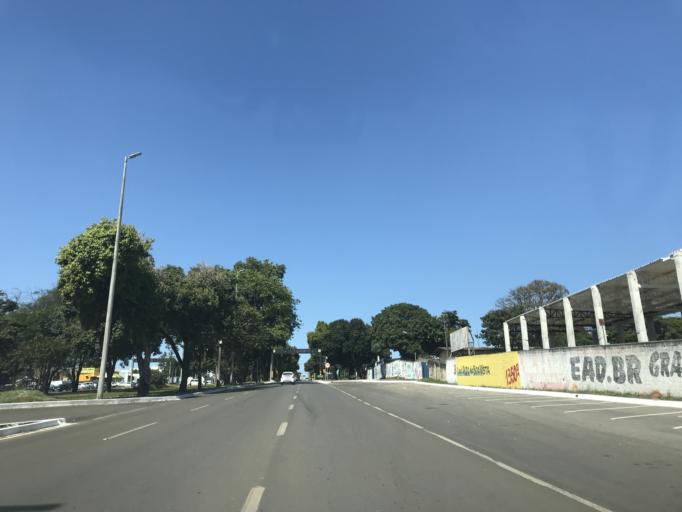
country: BR
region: Federal District
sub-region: Brasilia
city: Brasilia
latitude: -15.6471
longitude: -47.7866
